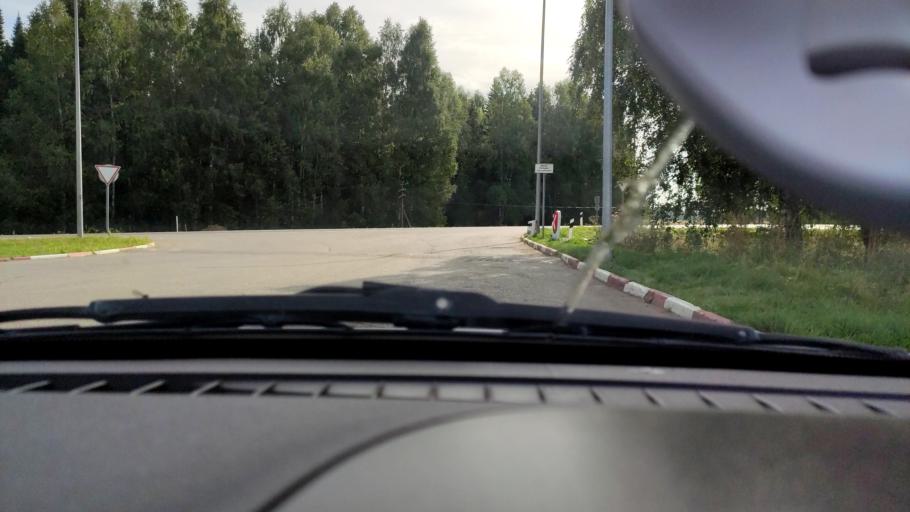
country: RU
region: Perm
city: Mendeleyevo
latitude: 58.1904
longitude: 54.9800
